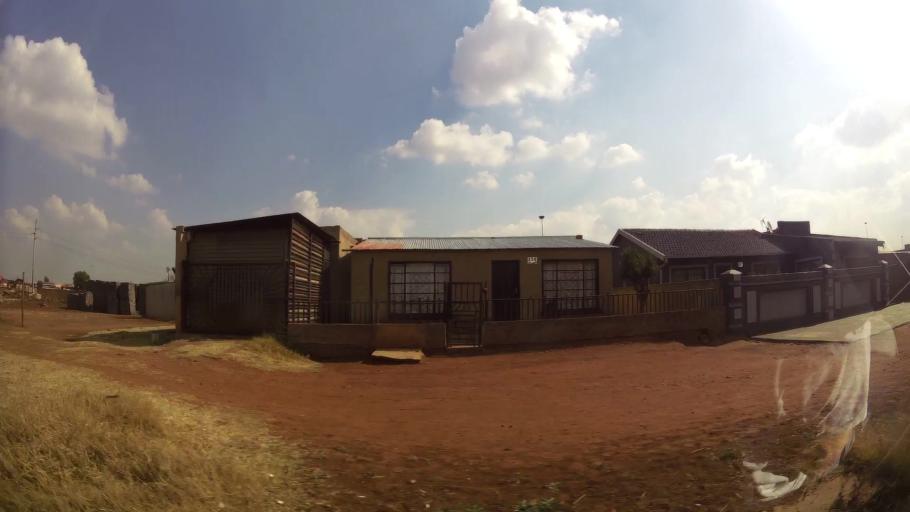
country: ZA
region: Gauteng
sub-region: Ekurhuleni Metropolitan Municipality
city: Germiston
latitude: -26.3581
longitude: 28.1653
